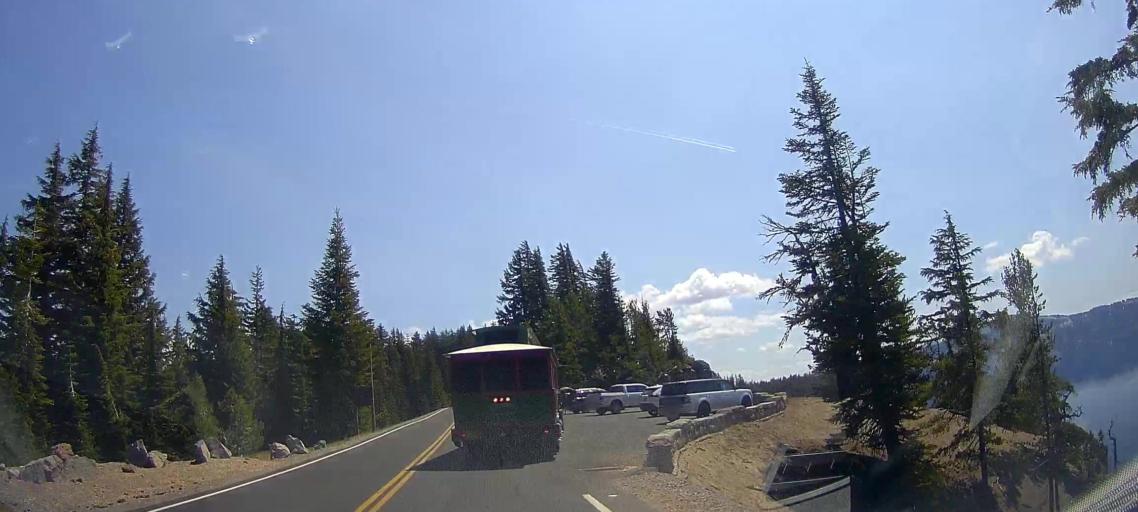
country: US
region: Oregon
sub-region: Jackson County
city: Shady Cove
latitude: 42.9800
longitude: -122.1152
